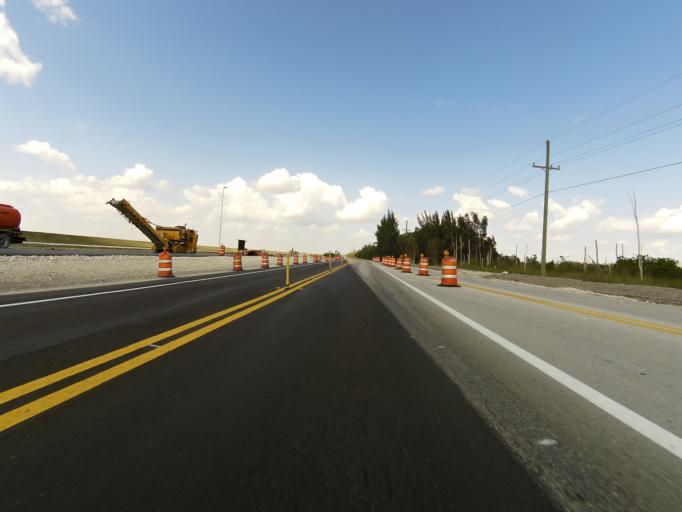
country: US
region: Florida
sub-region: Miami-Dade County
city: Palm Springs North
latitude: 25.9126
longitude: -80.4658
